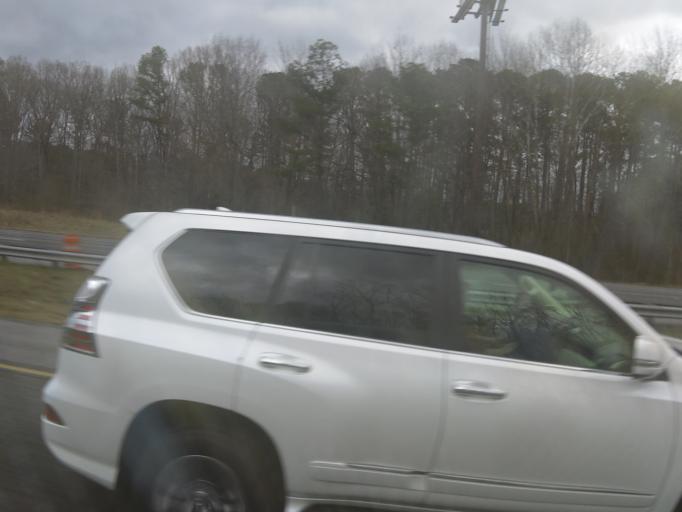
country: US
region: Georgia
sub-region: Whitfield County
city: Dalton
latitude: 34.6482
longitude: -84.9819
